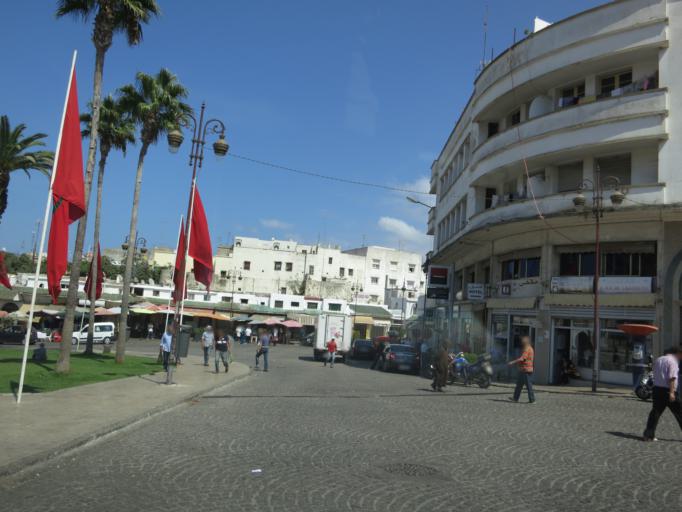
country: MA
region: Tanger-Tetouan
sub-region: Tanger-Assilah
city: Tangier
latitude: 35.7841
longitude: -5.8129
